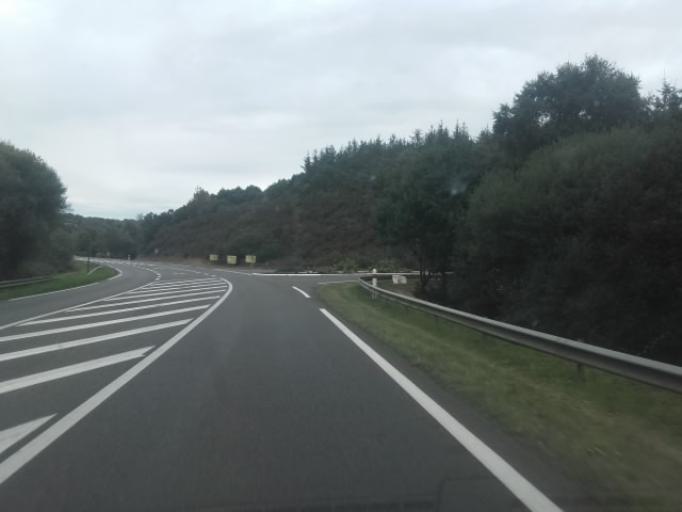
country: FR
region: Brittany
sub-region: Departement des Cotes-d'Armor
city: Lantic
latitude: 48.5721
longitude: -2.9011
